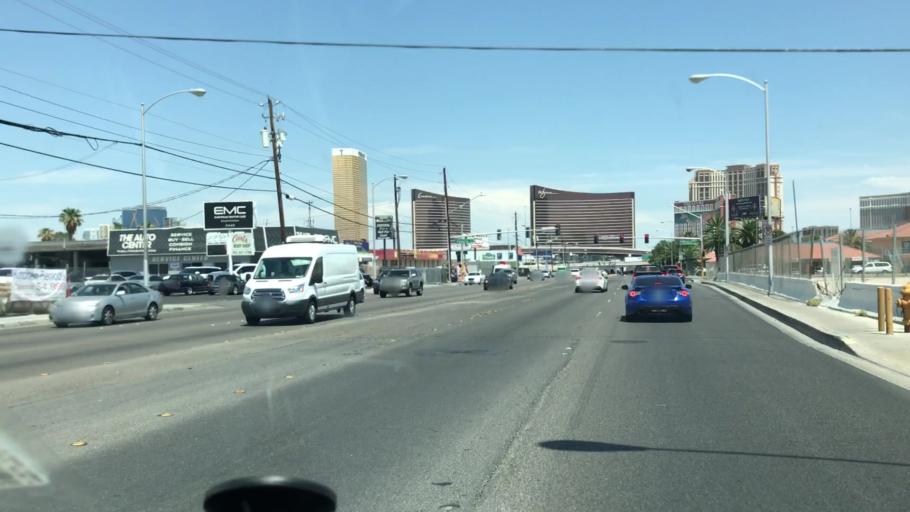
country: US
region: Nevada
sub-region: Clark County
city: Paradise
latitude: 36.1261
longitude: -115.1871
